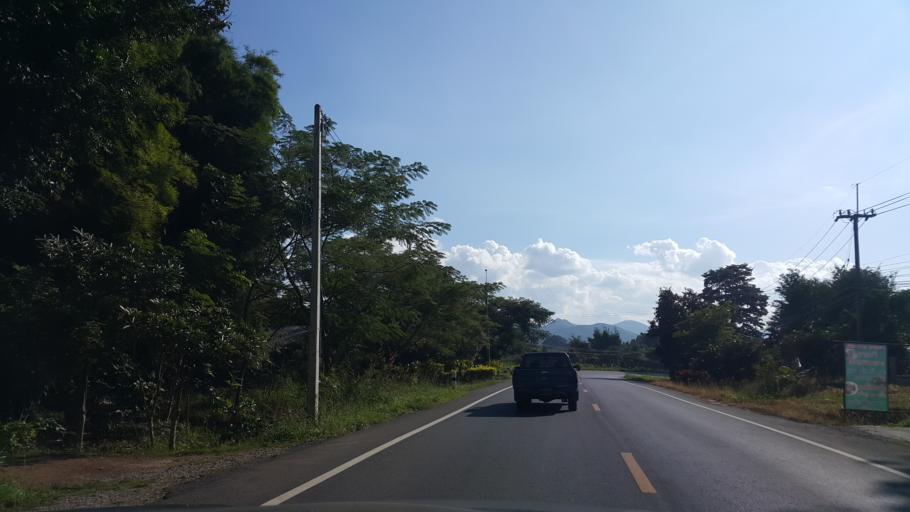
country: TH
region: Lamphun
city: Mae Tha
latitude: 18.5014
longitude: 99.1996
